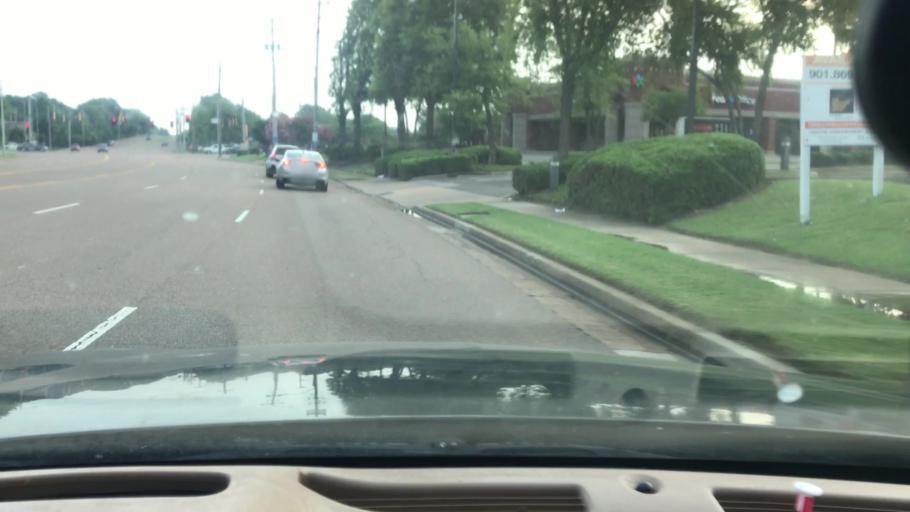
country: US
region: Tennessee
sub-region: Shelby County
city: Bartlett
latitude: 35.2033
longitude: -89.8643
